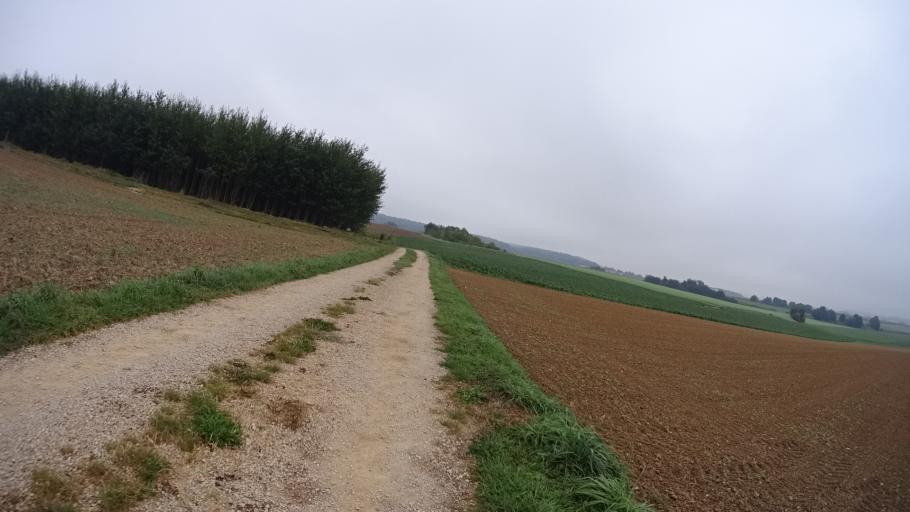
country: DE
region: Bavaria
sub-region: Upper Bavaria
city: Hepberg
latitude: 48.8247
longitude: 11.4756
